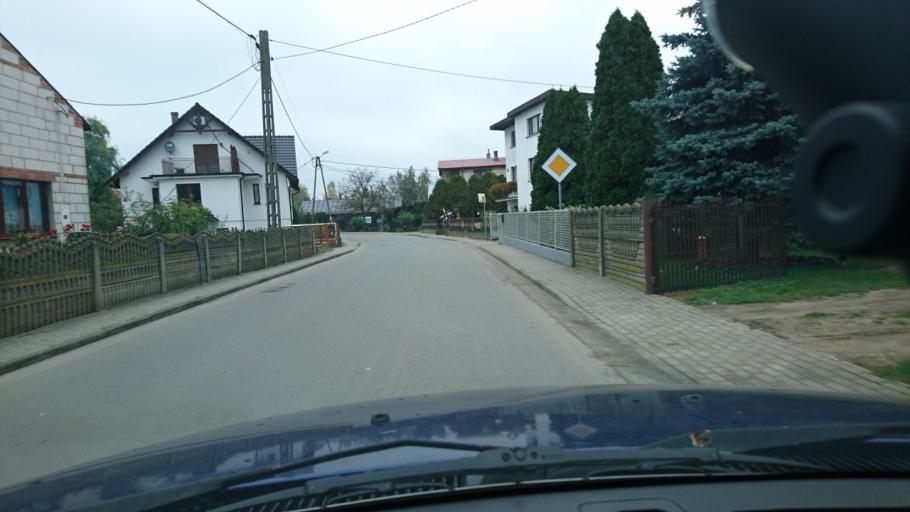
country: PL
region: Greater Poland Voivodeship
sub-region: Powiat krotoszynski
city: Sulmierzyce
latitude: 51.5674
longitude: 17.5890
